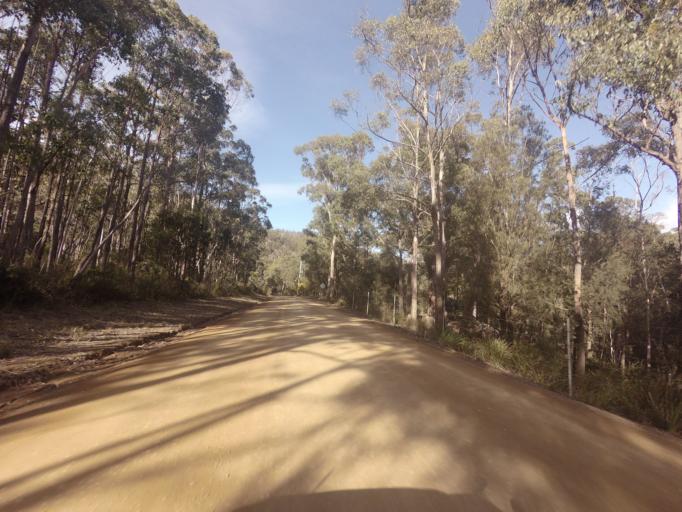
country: AU
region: Tasmania
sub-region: Huon Valley
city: Huonville
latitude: -43.0642
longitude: 147.0894
